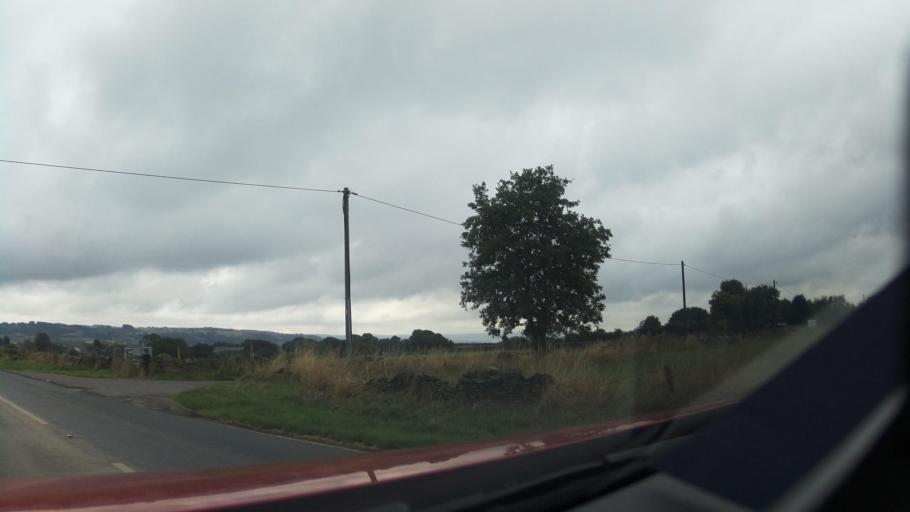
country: GB
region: England
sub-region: Kirklees
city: Shelley
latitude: 53.6023
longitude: -1.6810
